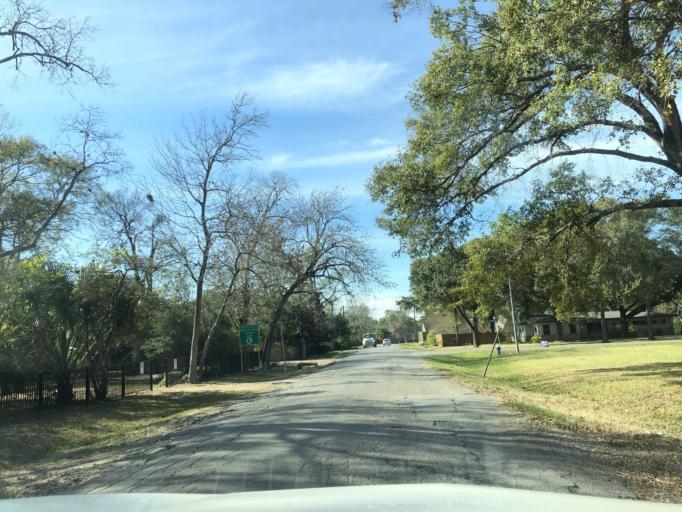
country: US
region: Texas
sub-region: Harris County
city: Bellaire
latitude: 29.6784
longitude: -95.5125
